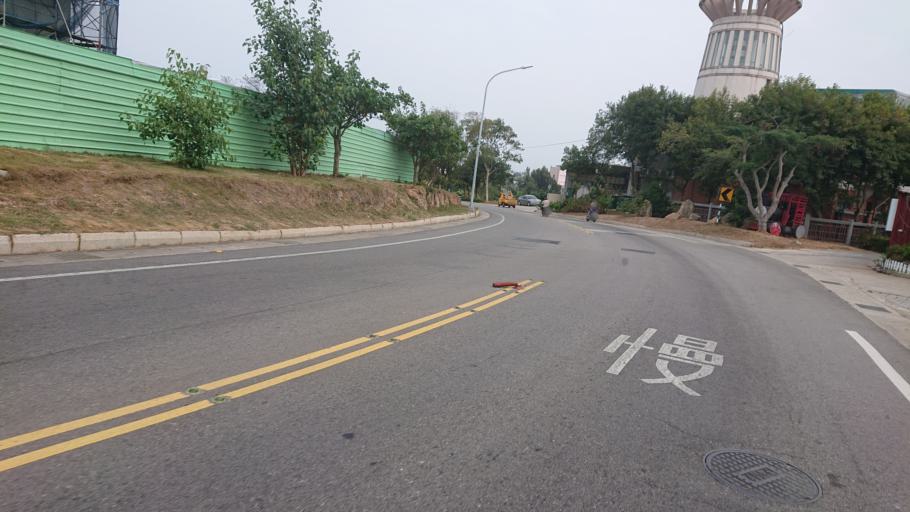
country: TW
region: Fukien
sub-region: Kinmen
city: Jincheng
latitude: 24.4194
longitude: 118.3109
